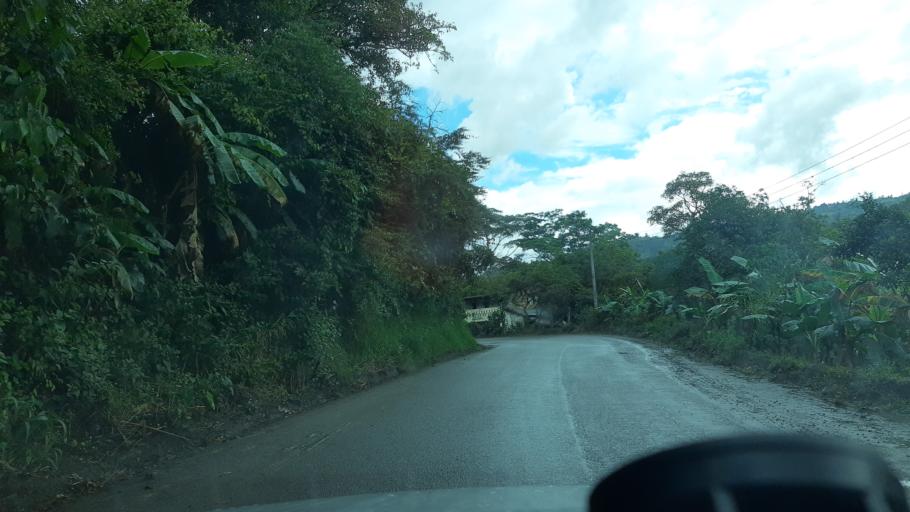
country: CO
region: Boyaca
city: Chinavita
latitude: 5.1330
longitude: -73.3631
